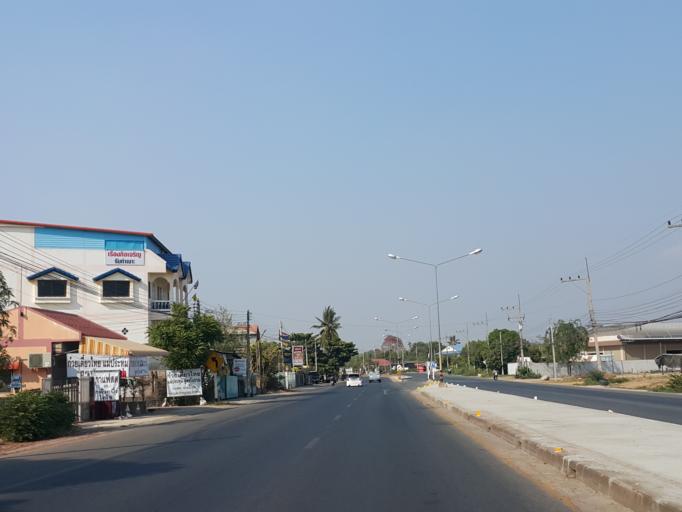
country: TH
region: Phitsanulok
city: Phitsanulok
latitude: 16.8341
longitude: 100.3353
